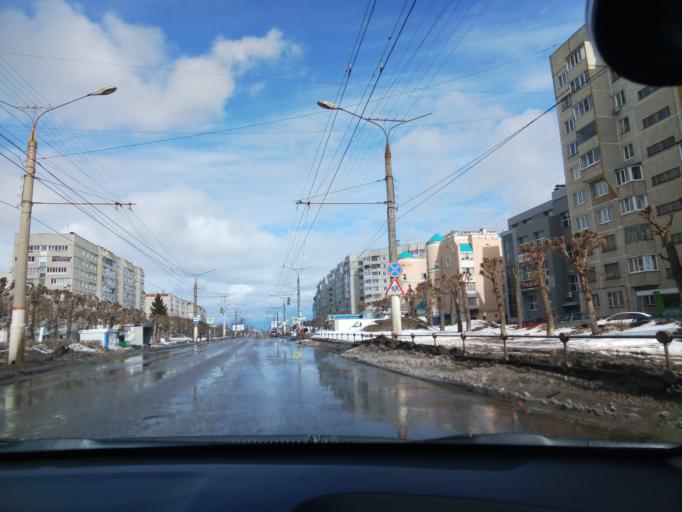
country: RU
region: Chuvashia
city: Novyye Lapsary
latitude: 56.1159
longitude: 47.1906
